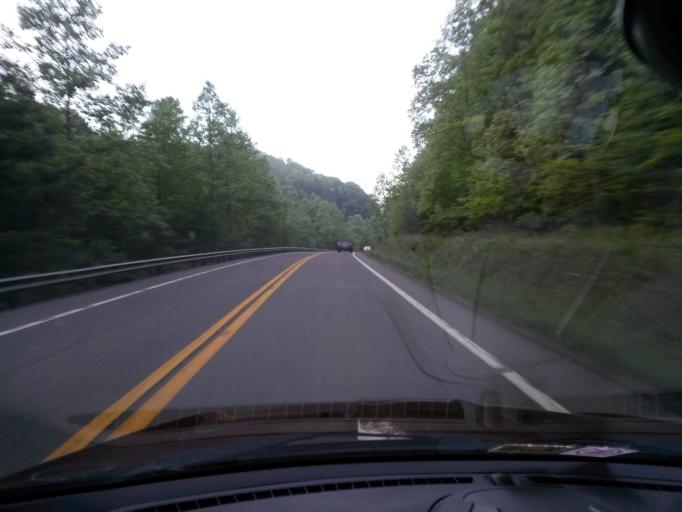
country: US
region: West Virginia
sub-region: Wyoming County
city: Pineville
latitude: 37.6245
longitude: -81.4802
